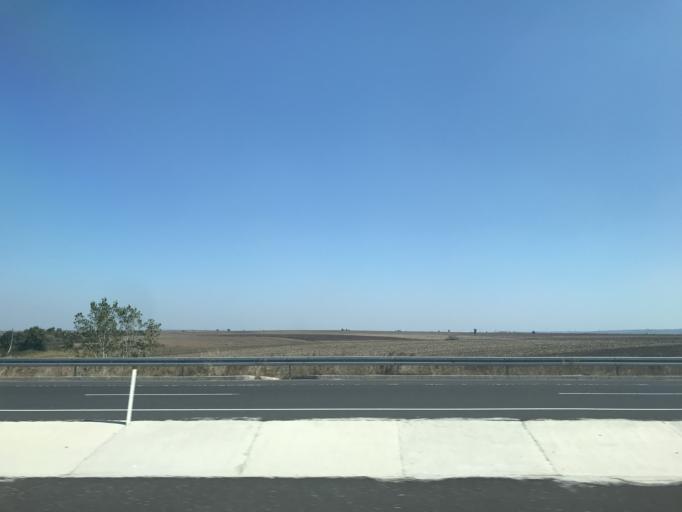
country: TR
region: Tekirdag
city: Muratli
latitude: 41.1789
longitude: 27.5387
